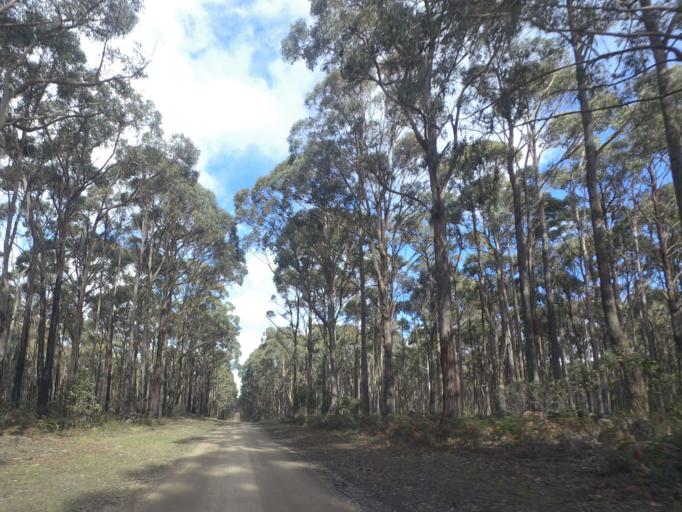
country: AU
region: Victoria
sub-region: Moorabool
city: Bacchus Marsh
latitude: -37.4310
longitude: 144.4655
